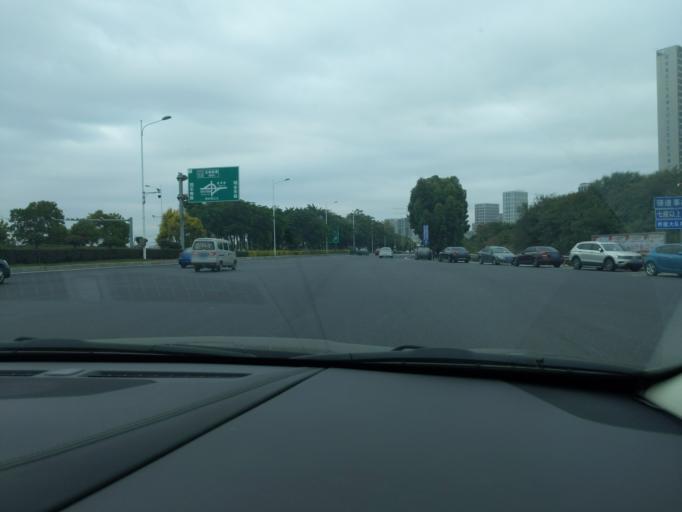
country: CN
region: Fujian
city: Liuwudian
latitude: 24.5675
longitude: 118.2240
